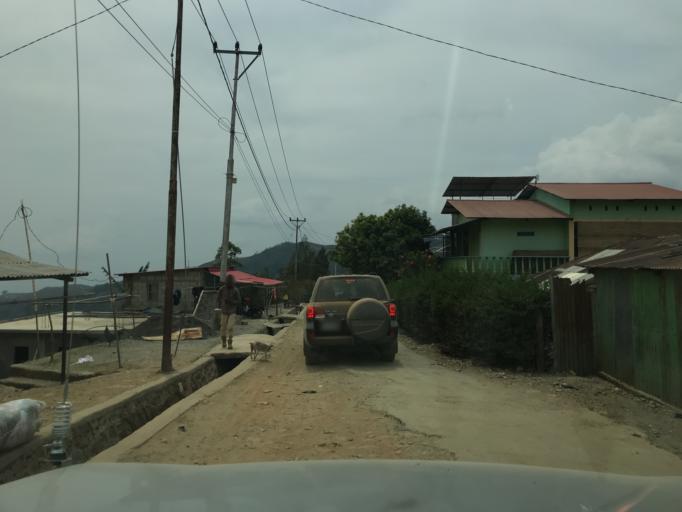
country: TL
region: Ermera
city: Gleno
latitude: -8.8371
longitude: 125.4305
